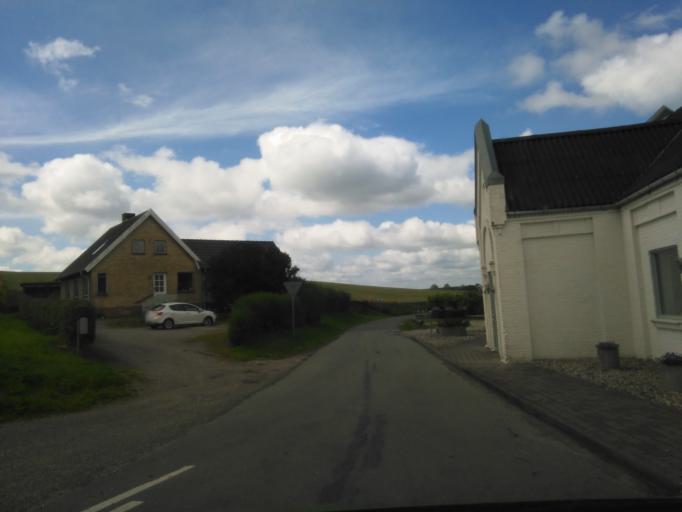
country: DK
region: Central Jutland
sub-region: Syddjurs Kommune
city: Ronde
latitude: 56.2421
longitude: 10.4925
